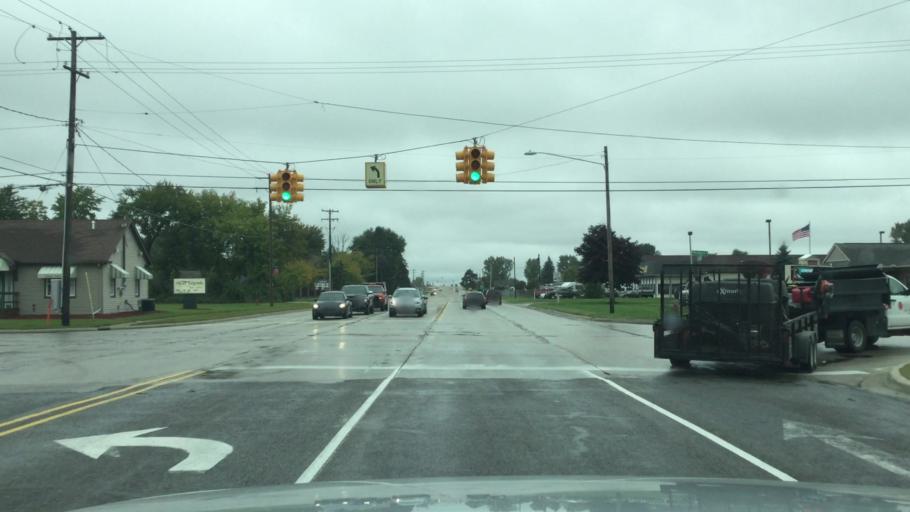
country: US
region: Michigan
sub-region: Saginaw County
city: Zilwaukee
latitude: 43.4797
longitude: -83.9455
